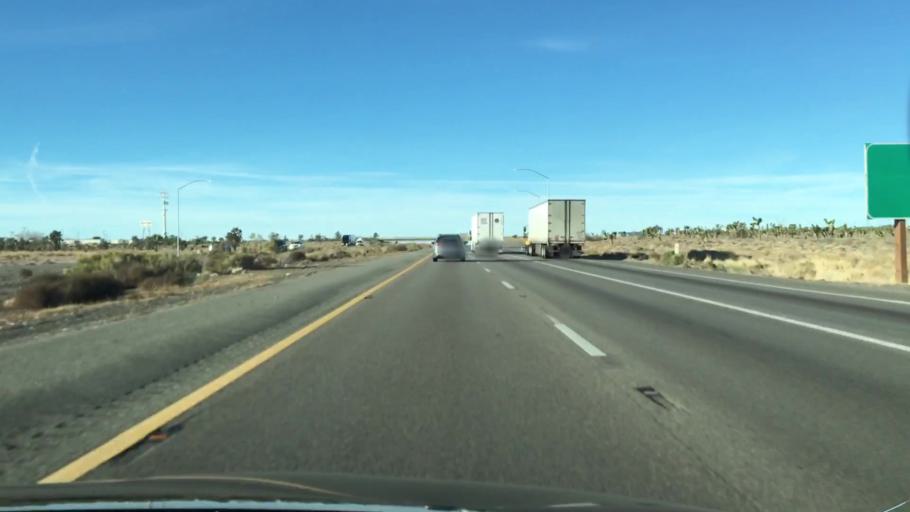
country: US
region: Nevada
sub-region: Clark County
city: Sandy Valley
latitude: 35.4051
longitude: -115.7854
